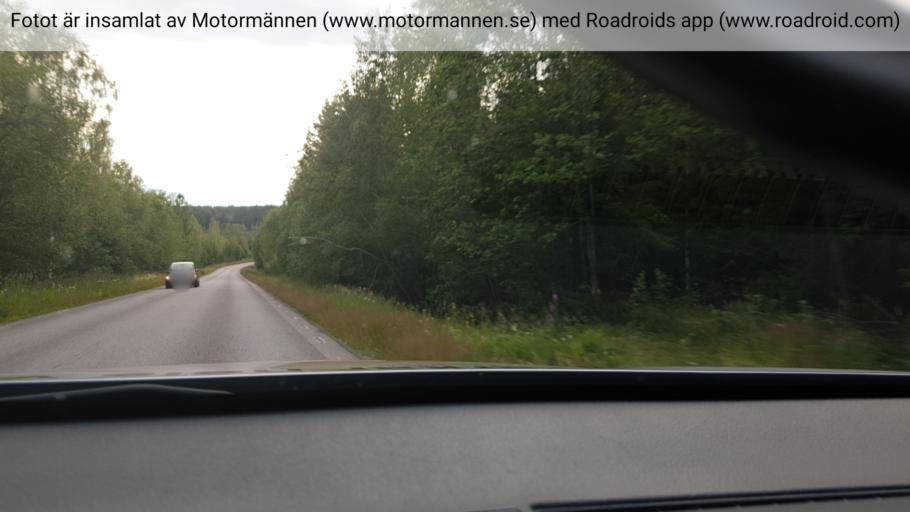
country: SE
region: Vaermland
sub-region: Forshaga Kommun
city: Deje
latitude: 59.7444
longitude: 13.3508
